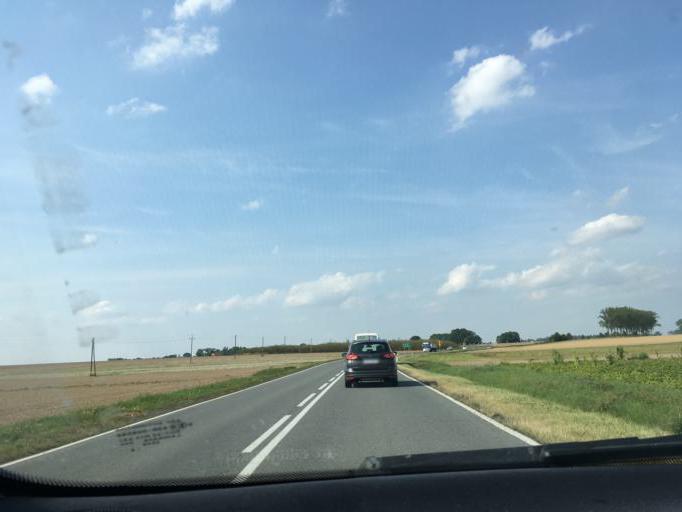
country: PL
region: Opole Voivodeship
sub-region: Powiat prudnicki
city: Prudnik
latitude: 50.3558
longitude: 17.5533
